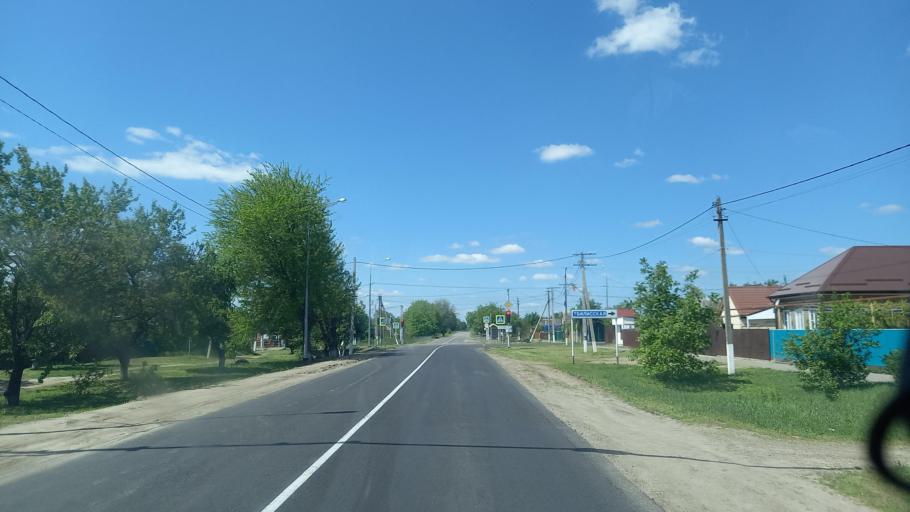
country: RU
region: Krasnodarskiy
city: Tbilisskaya
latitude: 45.3247
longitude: 40.2318
